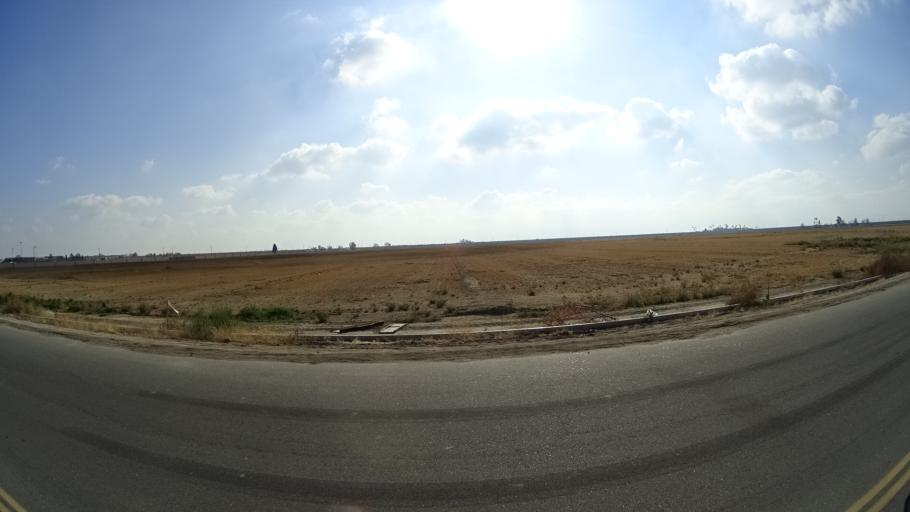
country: US
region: California
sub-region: Kern County
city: Greenacres
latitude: 35.2891
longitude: -119.1205
